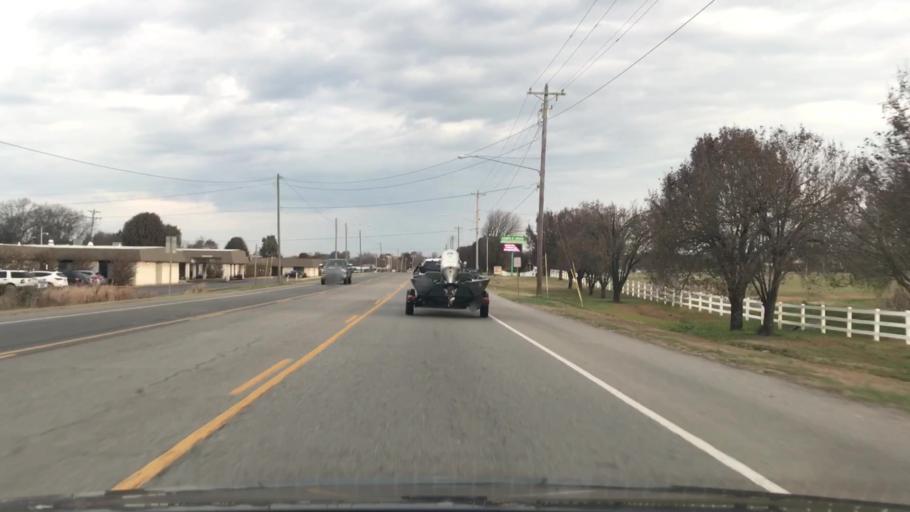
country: US
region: Tennessee
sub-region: Wilson County
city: Lebanon
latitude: 36.1977
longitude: -86.2755
